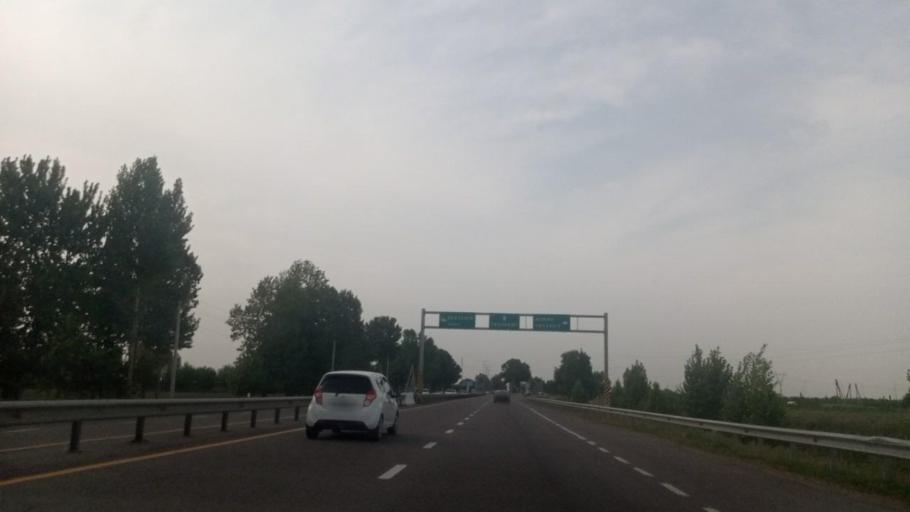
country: UZ
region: Toshkent Shahri
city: Bektemir
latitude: 41.1788
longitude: 69.4085
